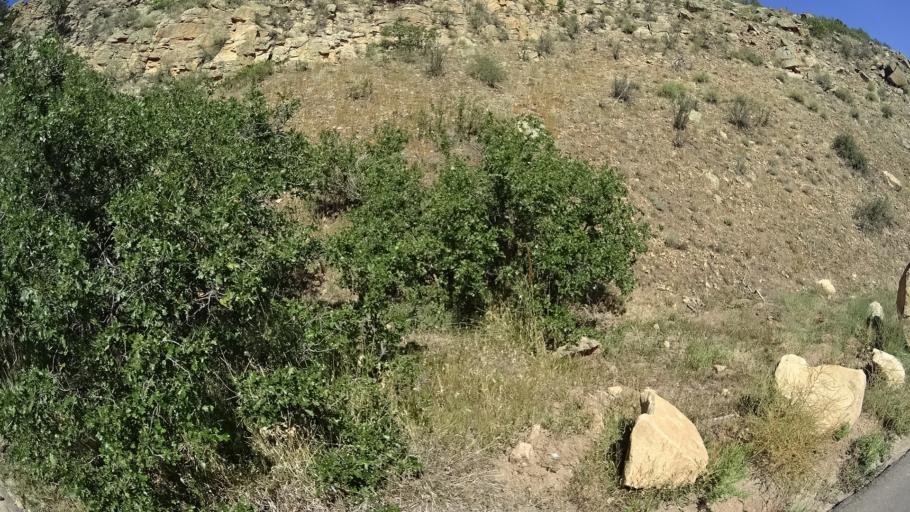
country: US
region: Colorado
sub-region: El Paso County
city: Manitou Springs
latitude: 38.8241
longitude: -104.8877
